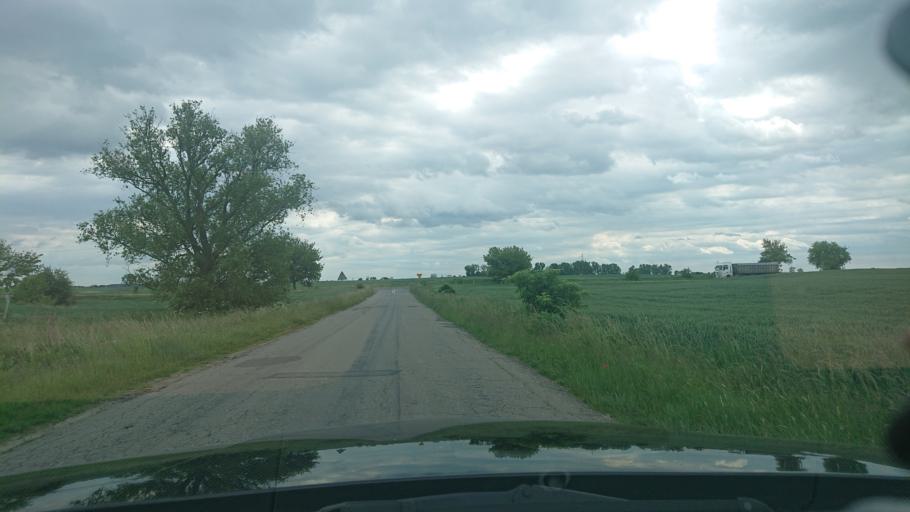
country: PL
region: Greater Poland Voivodeship
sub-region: Powiat gnieznienski
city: Gniezno
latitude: 52.5376
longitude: 17.5338
